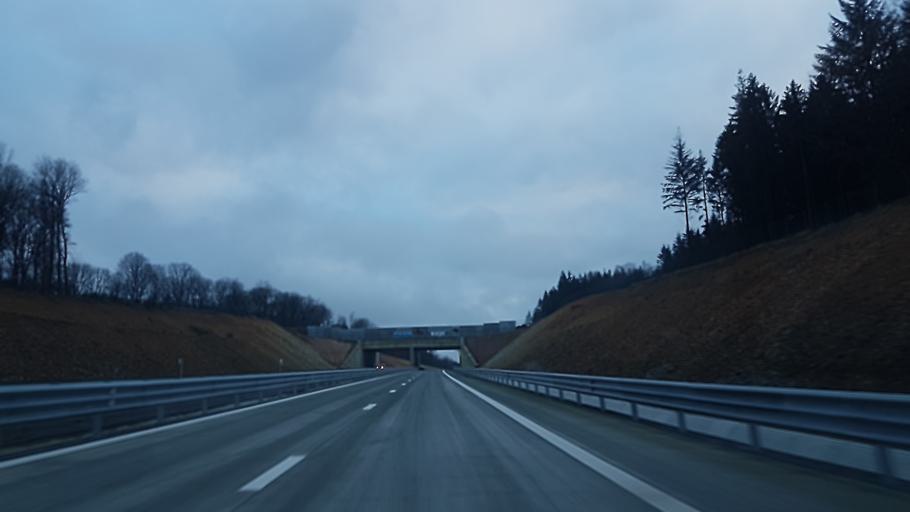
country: BE
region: Wallonia
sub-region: Province de Namur
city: Couvin
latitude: 50.0034
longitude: 4.5399
